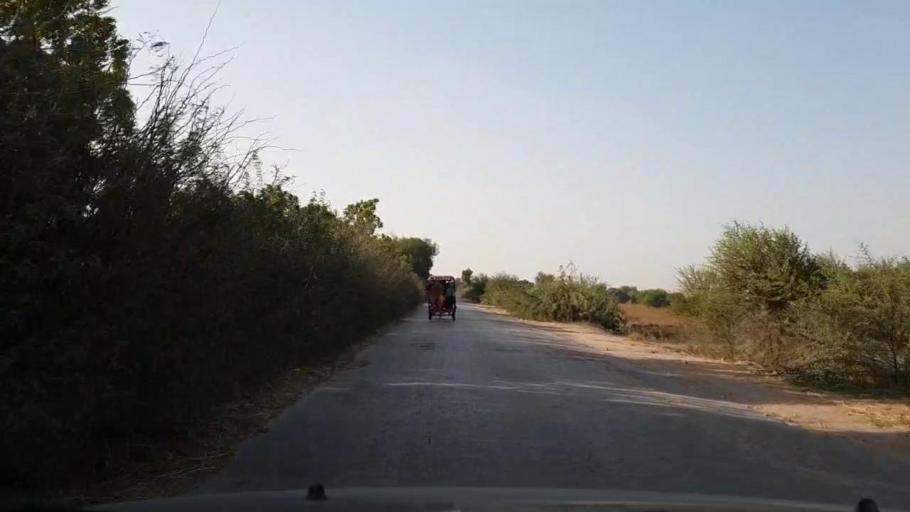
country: PK
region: Sindh
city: Tando Ghulam Ali
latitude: 25.1958
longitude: 68.8016
